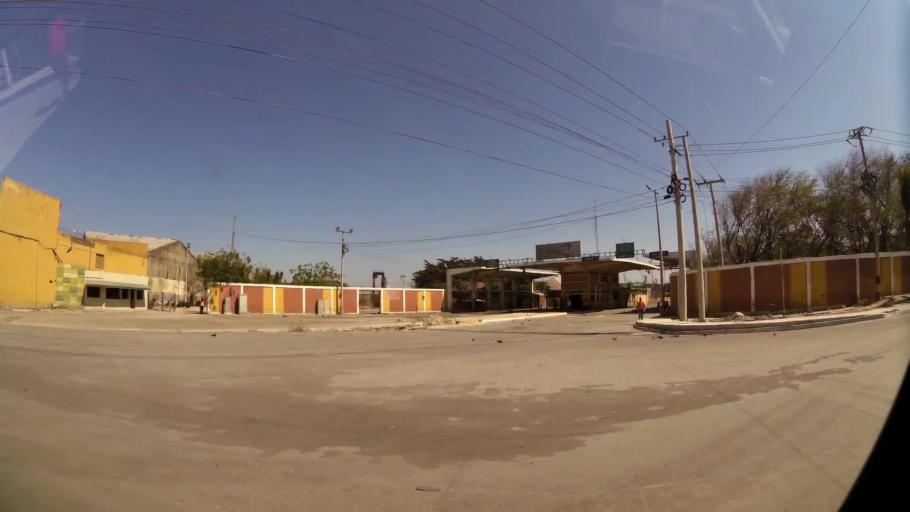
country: CO
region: Atlantico
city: Barranquilla
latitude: 10.9712
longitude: -74.7645
